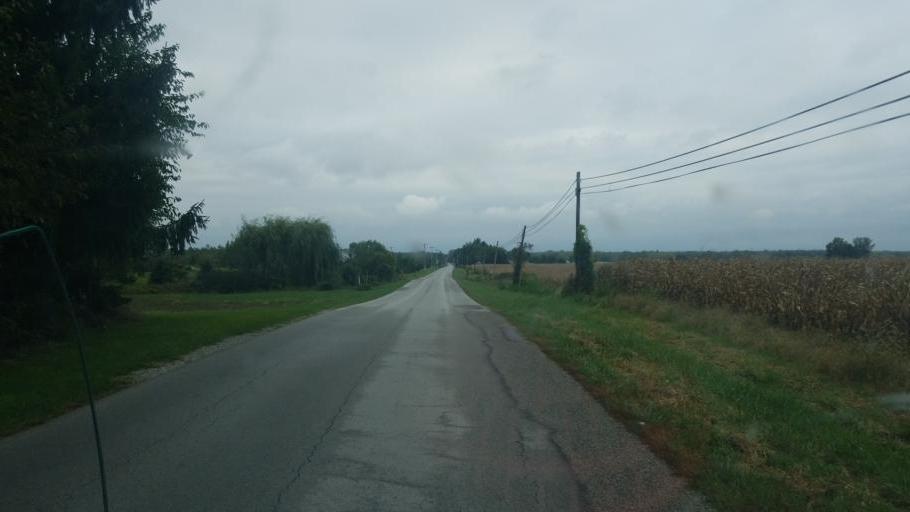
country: US
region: Ohio
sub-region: Wood County
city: Bowling Green
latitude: 41.2860
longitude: -83.6695
